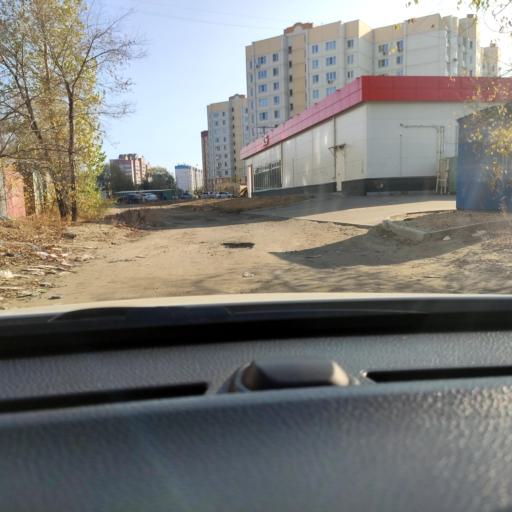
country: RU
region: Voronezj
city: Voronezh
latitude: 51.7207
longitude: 39.2623
